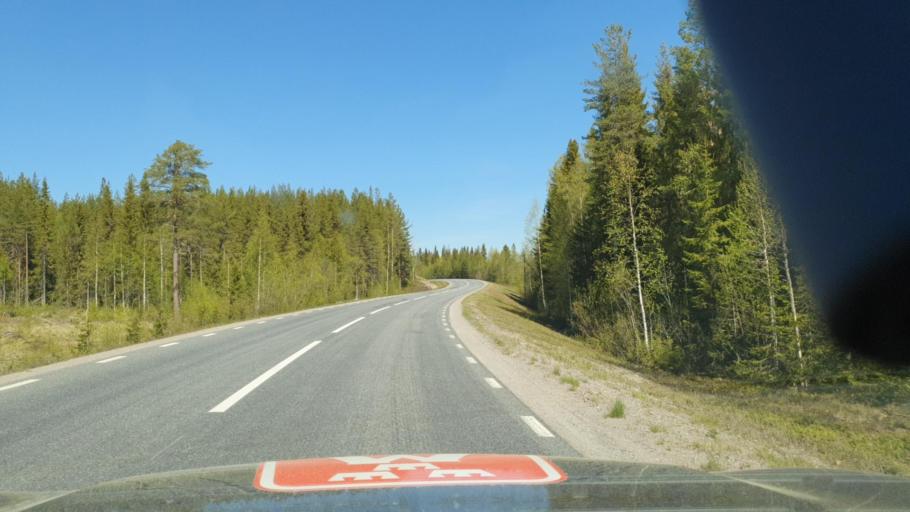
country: SE
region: Vaesternorrland
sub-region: OErnskoeldsviks Kommun
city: Bredbyn
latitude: 63.7289
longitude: 18.5002
